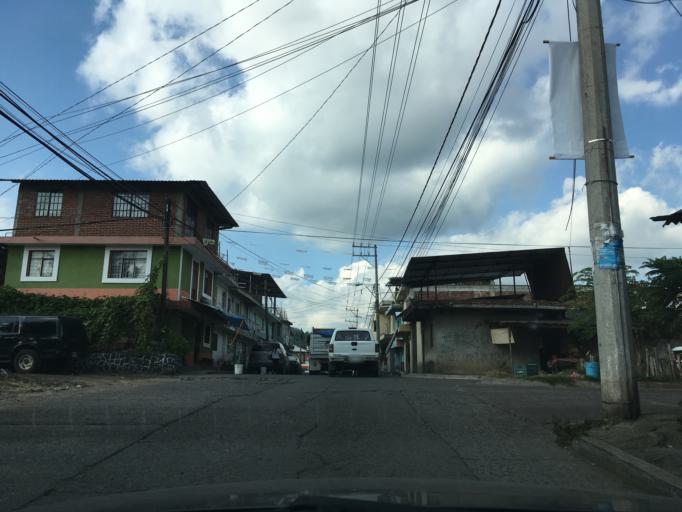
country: MX
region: Michoacan
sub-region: Uruapan
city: Uruapan
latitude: 19.4295
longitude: -102.0787
